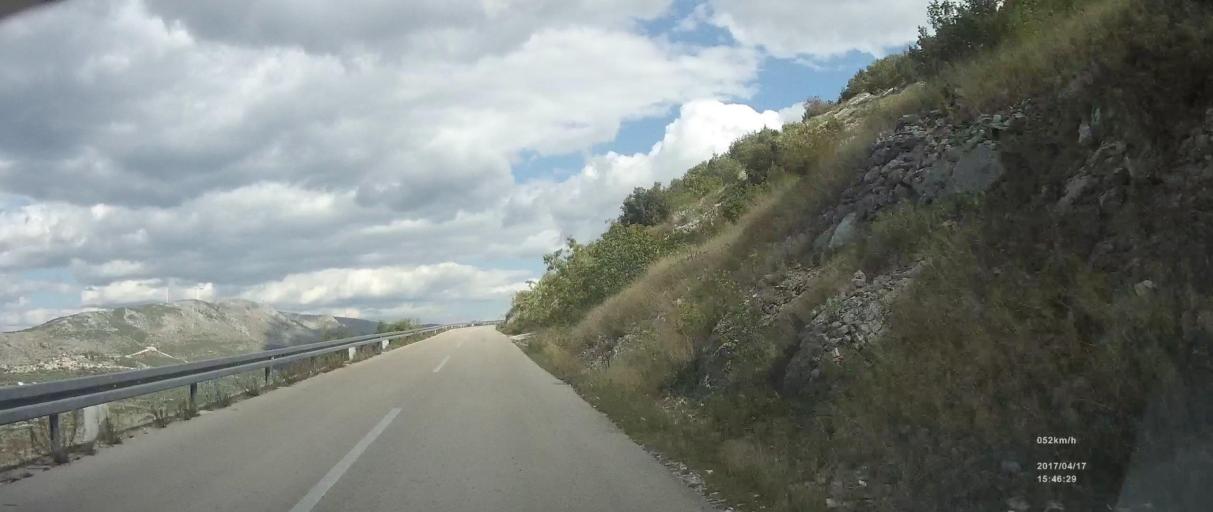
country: HR
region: Sibensko-Kniniska
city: Primosten
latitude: 43.6268
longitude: 15.9698
